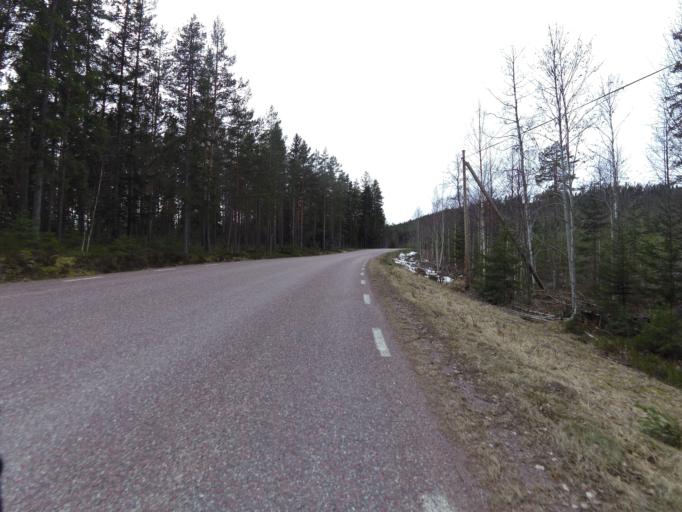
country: SE
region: Gaevleborg
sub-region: Hofors Kommun
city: Hofors
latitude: 60.4910
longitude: 16.4254
